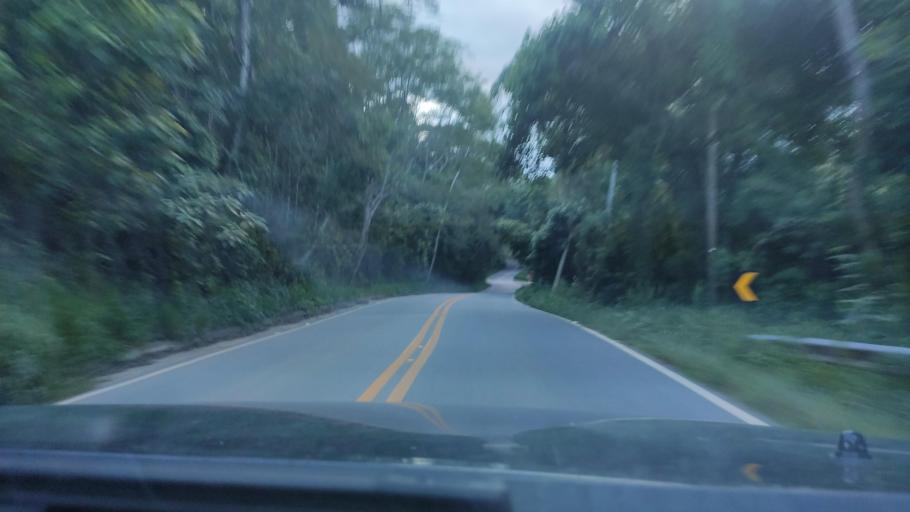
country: BR
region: Sao Paulo
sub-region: Campos Do Jordao
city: Campos do Jordao
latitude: -22.8258
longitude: -45.6794
